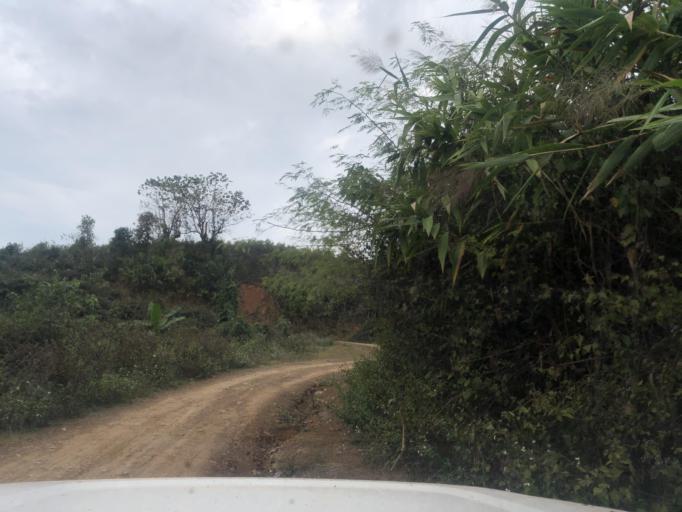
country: LA
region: Phongsali
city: Khoa
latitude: 21.3082
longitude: 102.5837
